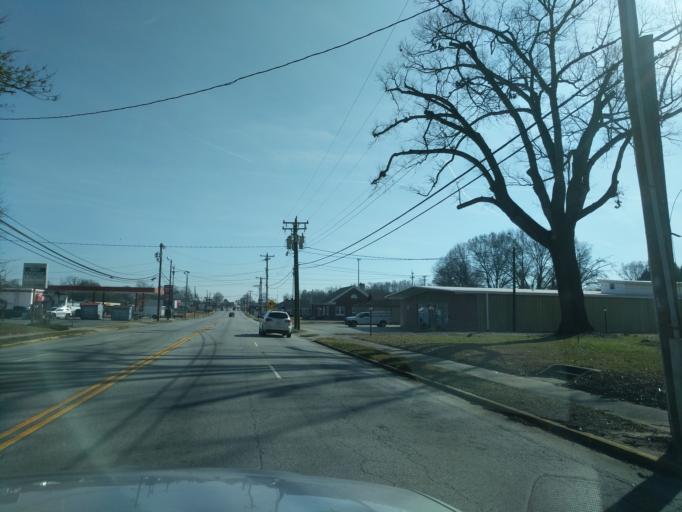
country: US
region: South Carolina
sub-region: Spartanburg County
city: Woodruff
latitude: 34.7466
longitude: -82.0443
